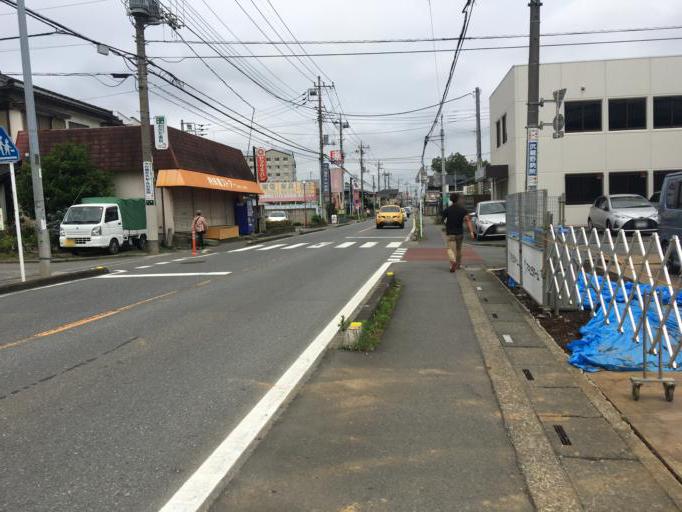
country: JP
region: Saitama
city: Ageoshimo
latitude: 35.9614
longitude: 139.5994
